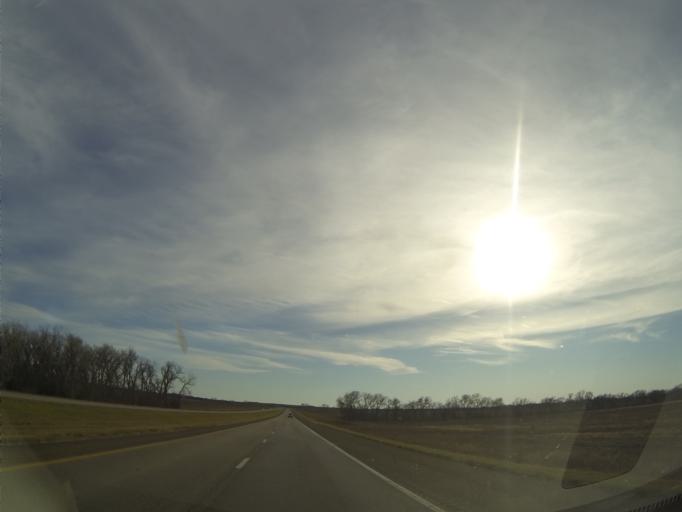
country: US
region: Kansas
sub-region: Ottawa County
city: Minneapolis
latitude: 39.0682
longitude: -97.6499
